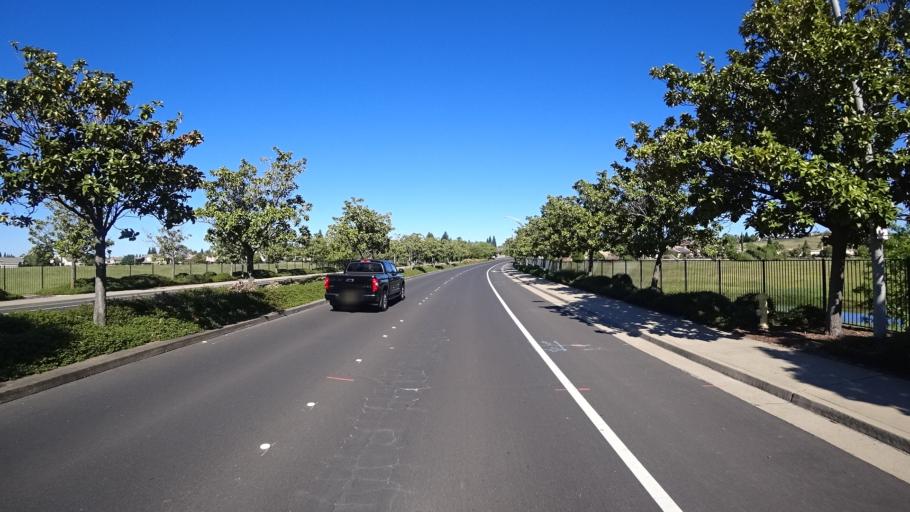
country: US
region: California
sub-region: Placer County
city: Rocklin
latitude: 38.8149
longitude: -121.2665
